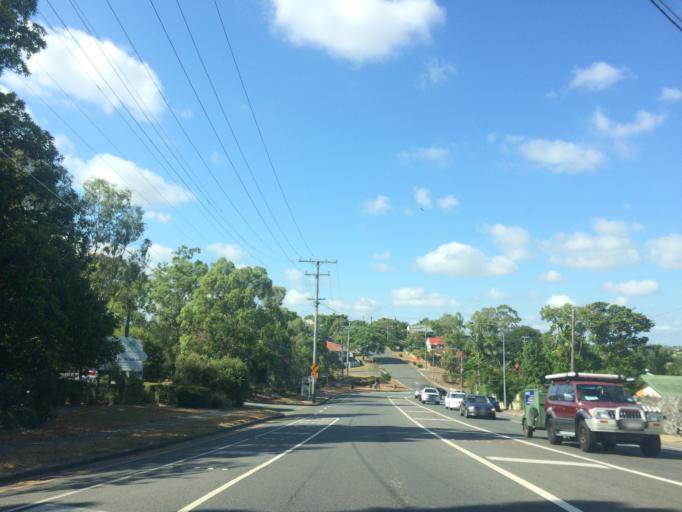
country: AU
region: Queensland
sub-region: Brisbane
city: Seven Hills
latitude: -27.4767
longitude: 153.0664
